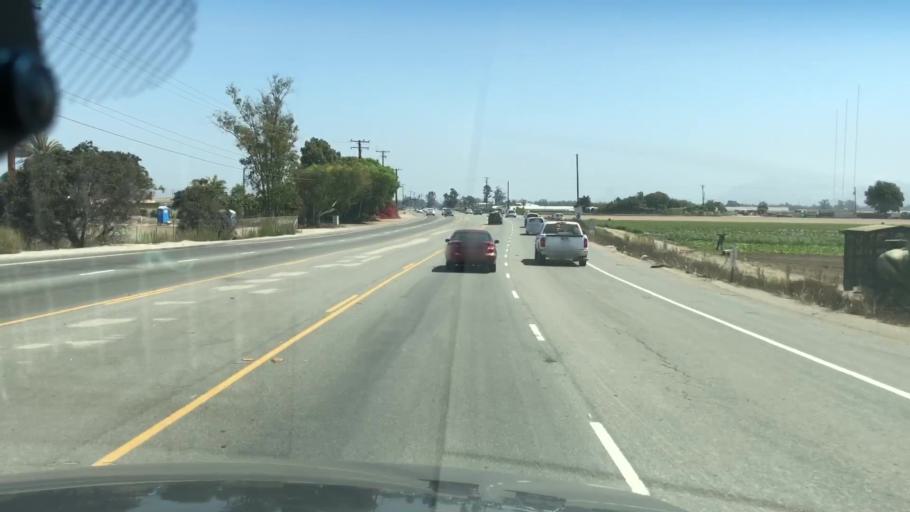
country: US
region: California
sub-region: Ventura County
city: Oxnard
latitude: 34.1674
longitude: -119.1400
